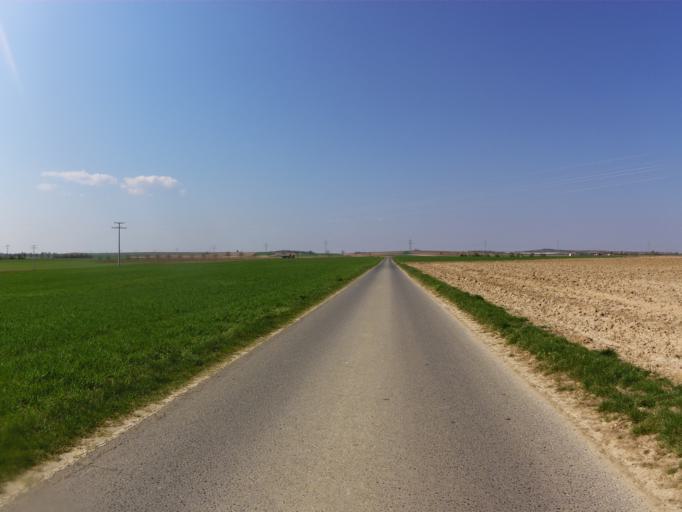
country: DE
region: Bavaria
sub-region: Regierungsbezirk Unterfranken
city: Mainstockheim
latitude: 49.8139
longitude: 10.1110
